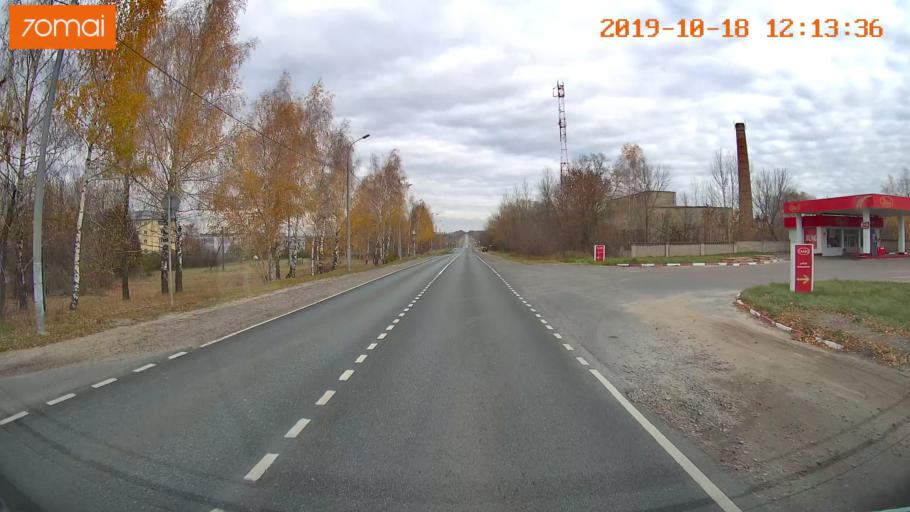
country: RU
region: Rjazan
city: Zakharovo
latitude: 54.4221
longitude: 39.3716
